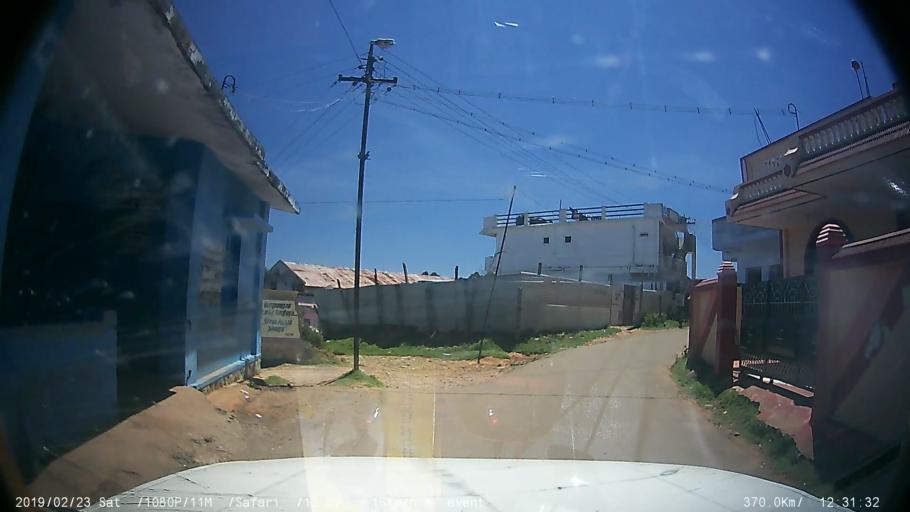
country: IN
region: Tamil Nadu
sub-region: Nilgiri
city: Wellington
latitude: 11.3492
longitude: 76.7801
